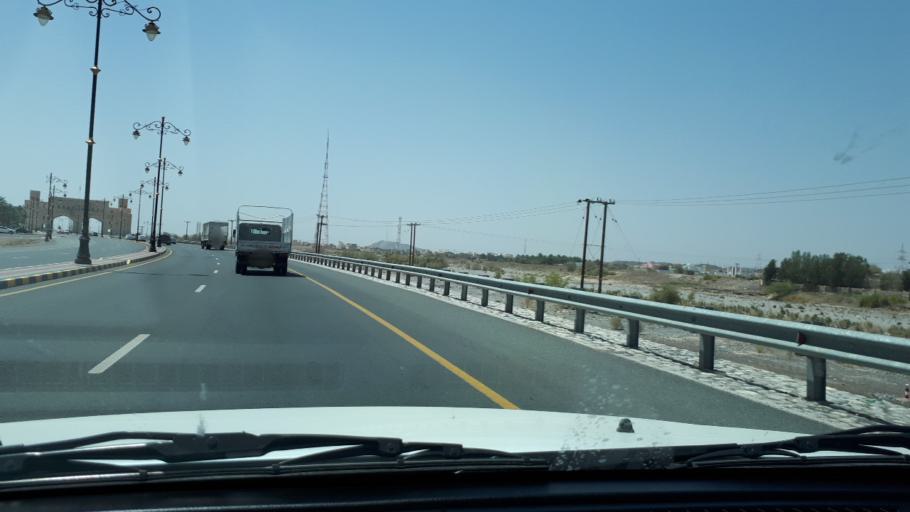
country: OM
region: Muhafazat ad Dakhiliyah
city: Nizwa
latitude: 22.8820
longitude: 57.5254
